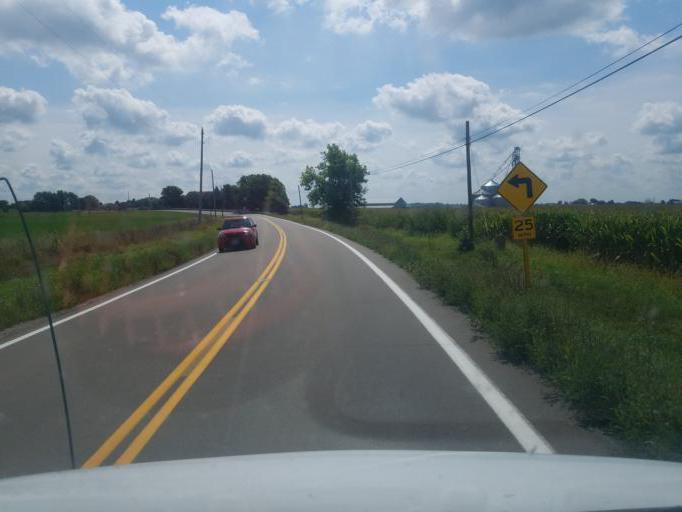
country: US
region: Ohio
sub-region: Marion County
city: Prospect
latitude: 40.3960
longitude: -83.1615
